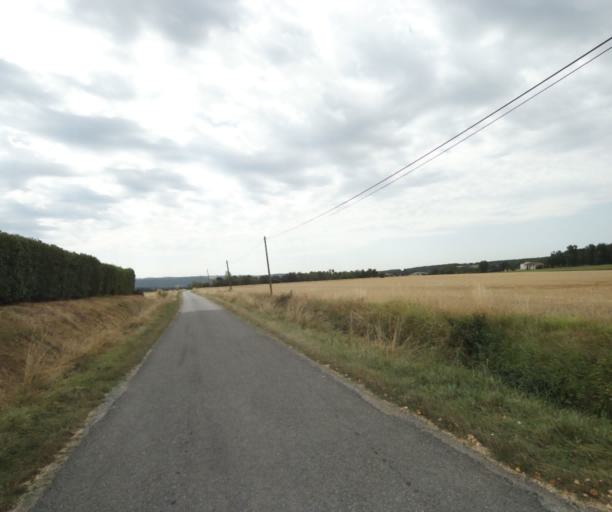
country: FR
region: Midi-Pyrenees
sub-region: Departement de la Haute-Garonne
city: Saint-Felix-Lauragais
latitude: 43.4415
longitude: 1.9275
